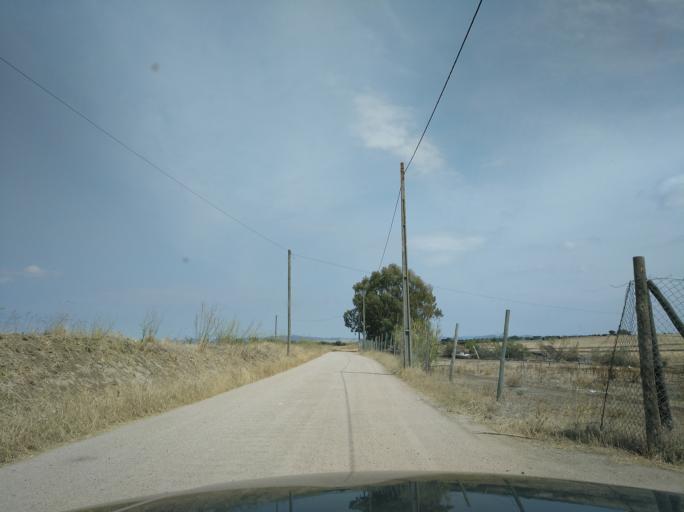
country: PT
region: Portalegre
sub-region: Campo Maior
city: Campo Maior
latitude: 39.0291
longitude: -7.0649
